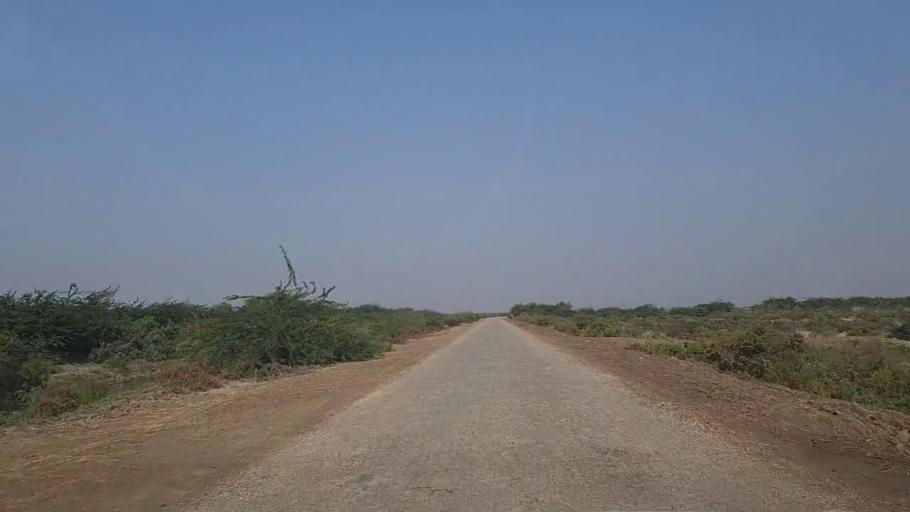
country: PK
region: Sindh
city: Keti Bandar
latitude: 24.2371
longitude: 67.6833
